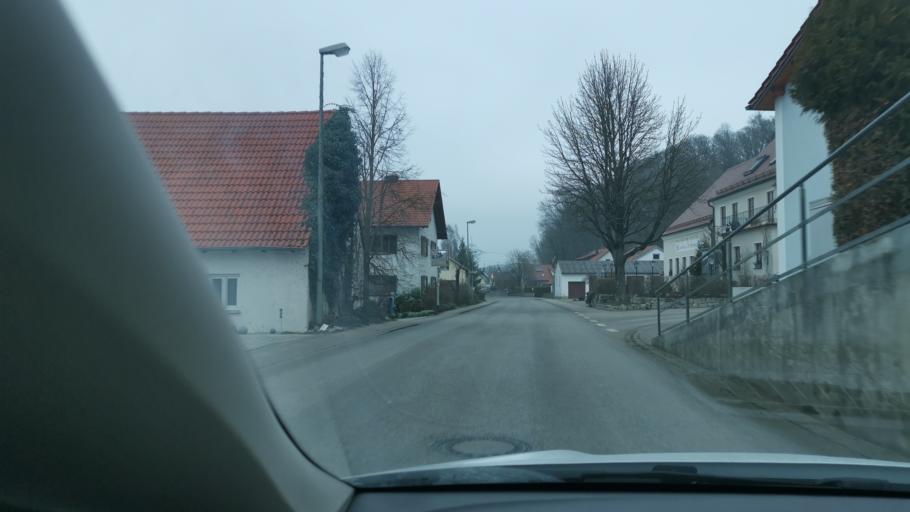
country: DE
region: Bavaria
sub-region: Swabia
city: Rehling
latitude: 48.4937
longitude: 10.9214
